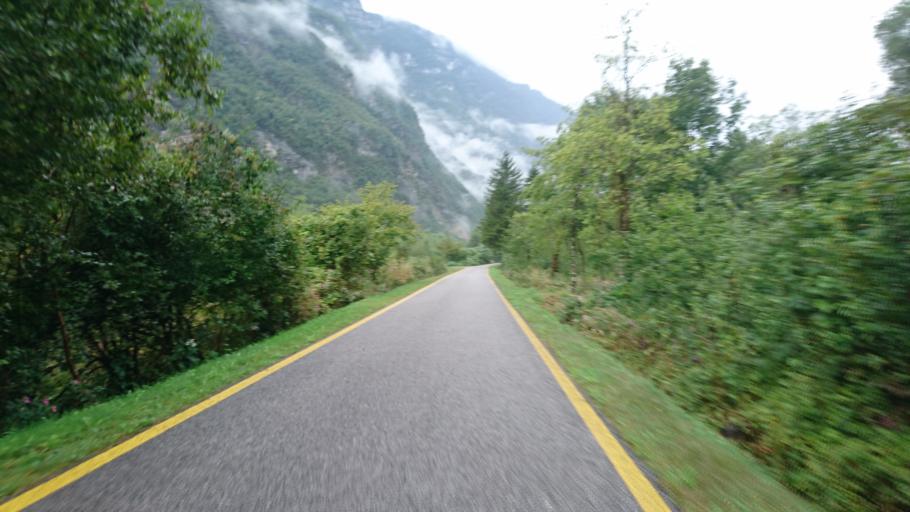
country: IT
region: Trentino-Alto Adige
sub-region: Provincia di Trento
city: Grigno
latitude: 46.0111
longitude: 11.6238
